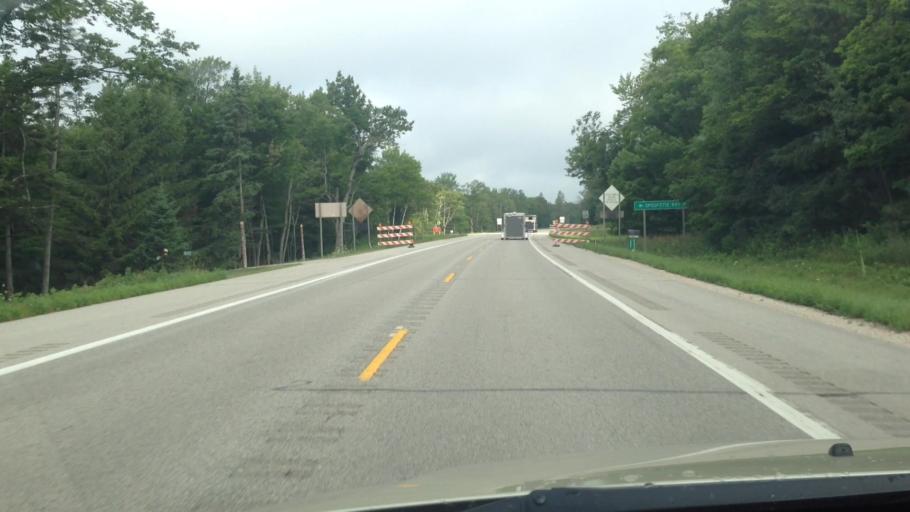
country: US
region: Michigan
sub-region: Luce County
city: Newberry
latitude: 46.0548
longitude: -85.1563
